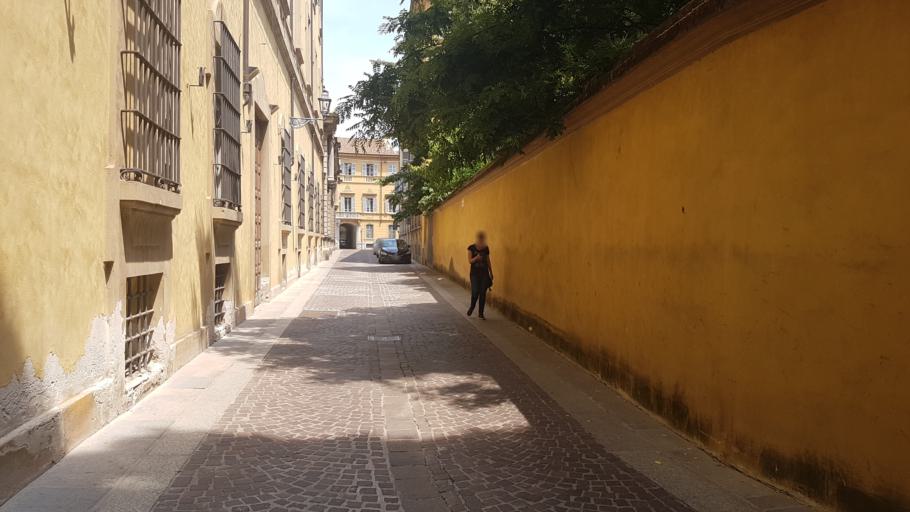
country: IT
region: Emilia-Romagna
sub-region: Provincia di Piacenza
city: Piacenza
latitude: 45.0519
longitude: 9.6898
